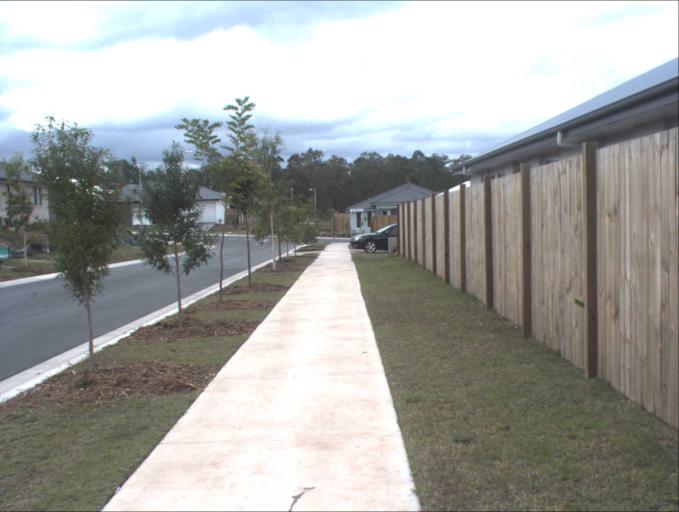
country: AU
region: Queensland
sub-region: Logan
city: Chambers Flat
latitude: -27.7973
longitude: 153.1070
